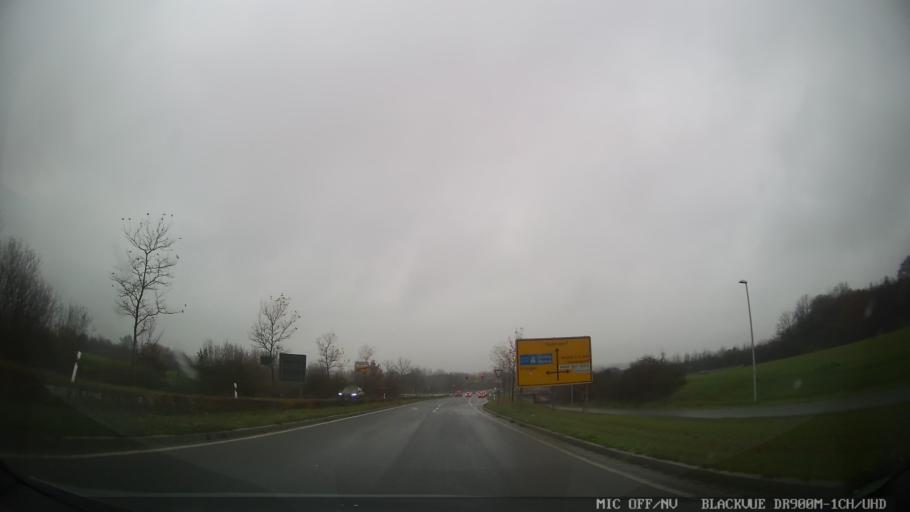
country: DE
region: Bavaria
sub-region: Regierungsbezirk Mittelfranken
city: Herzogenaurach
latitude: 49.5711
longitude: 10.9126
